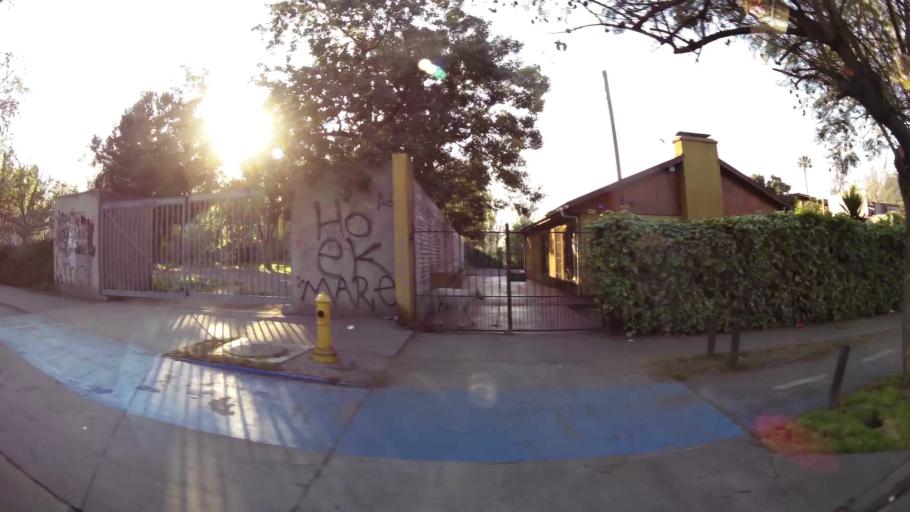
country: CL
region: Santiago Metropolitan
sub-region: Provincia de Santiago
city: Santiago
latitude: -33.3772
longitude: -70.6379
